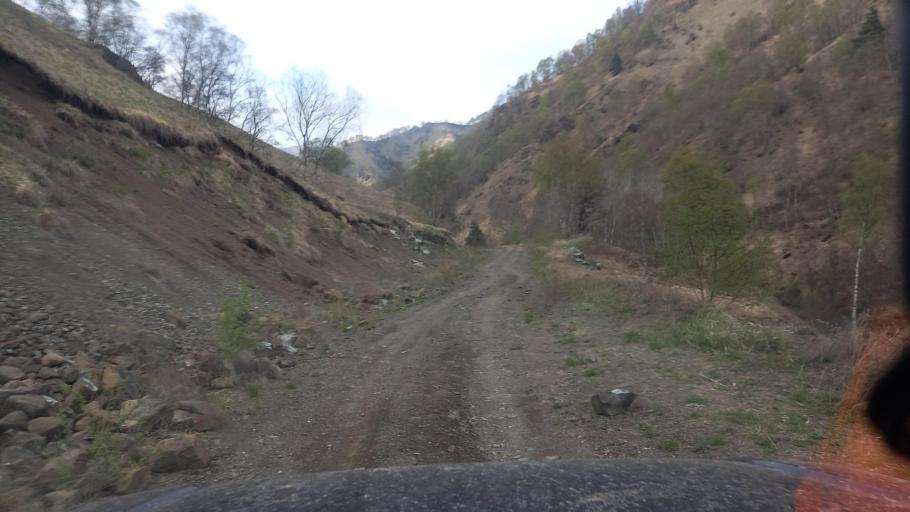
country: RU
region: Kabardino-Balkariya
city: Kamennomostskoye
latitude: 43.7037
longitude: 42.8443
